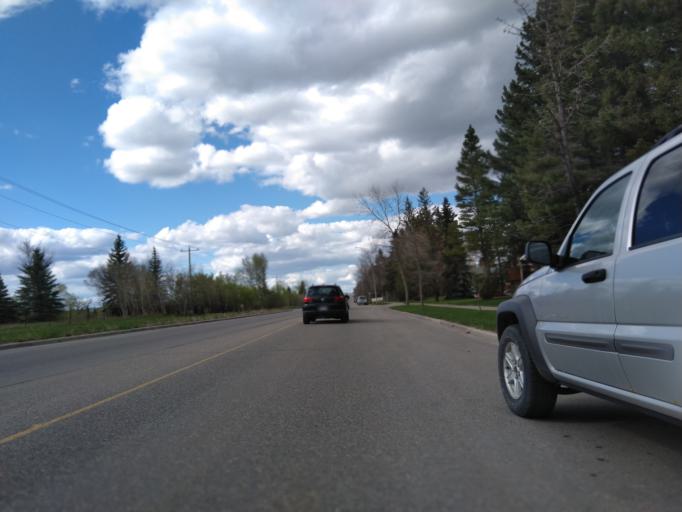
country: CA
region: Alberta
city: Calgary
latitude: 50.9957
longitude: -114.1410
